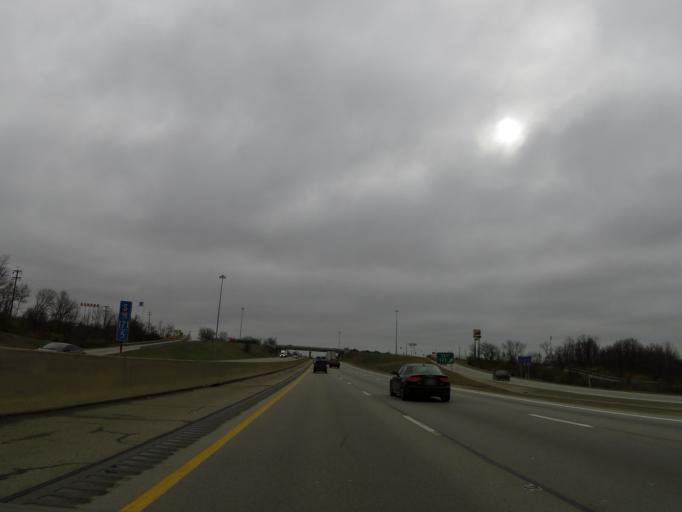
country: US
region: Kentucky
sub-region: Boone County
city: Walton
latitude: 38.8624
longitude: -84.6235
